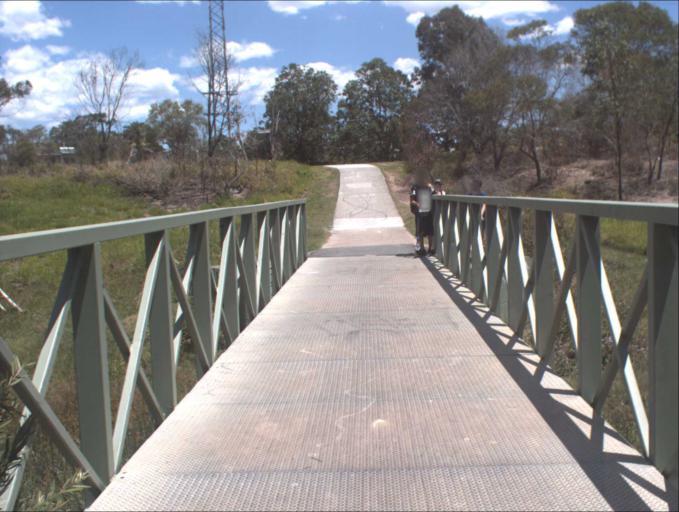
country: AU
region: Queensland
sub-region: Logan
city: Logan City
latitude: -27.6682
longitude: 153.1073
